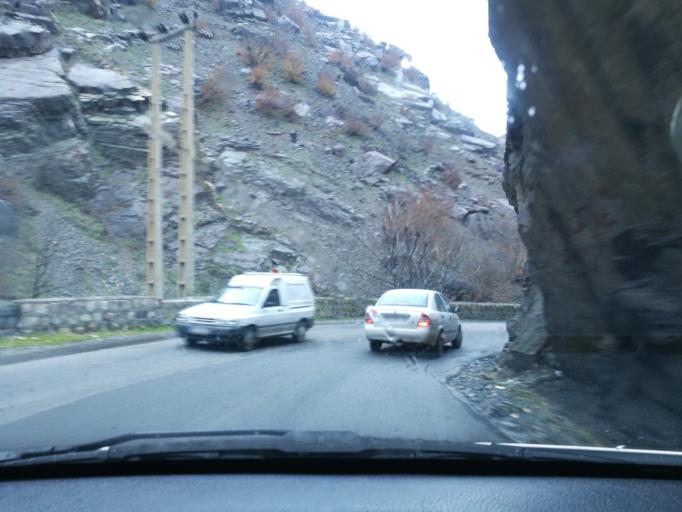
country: IR
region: Mazandaran
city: Chalus
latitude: 36.2797
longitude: 51.2424
